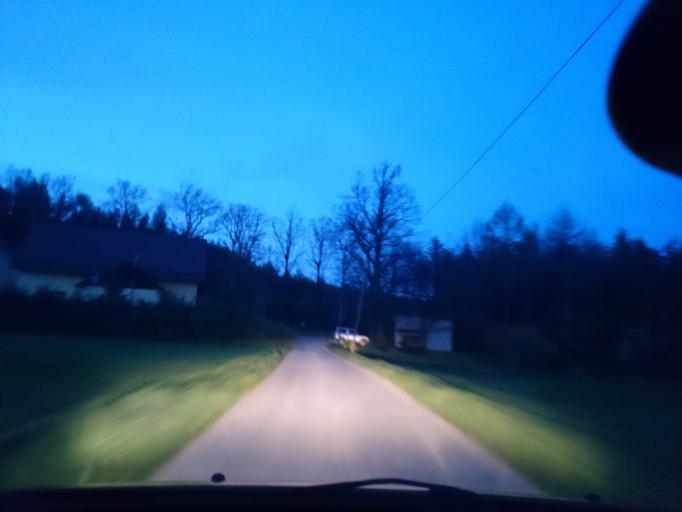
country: PL
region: Lower Silesian Voivodeship
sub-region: Powiat zabkowicki
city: Budzow
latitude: 50.5504
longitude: 16.7186
